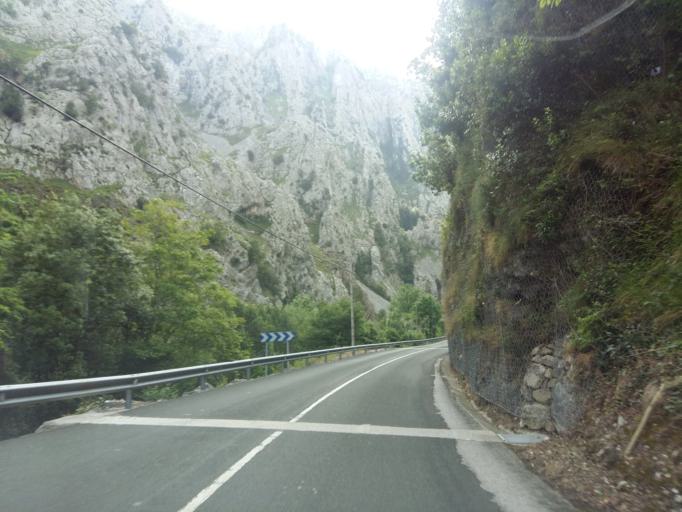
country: ES
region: Cantabria
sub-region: Provincia de Cantabria
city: Tresviso
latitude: 43.2650
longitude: -4.6262
